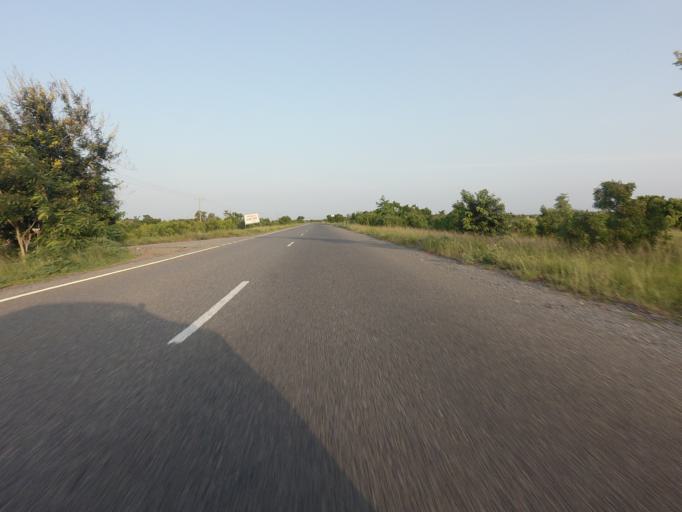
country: GH
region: Volta
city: Anloga
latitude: 5.8823
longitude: 0.7269
